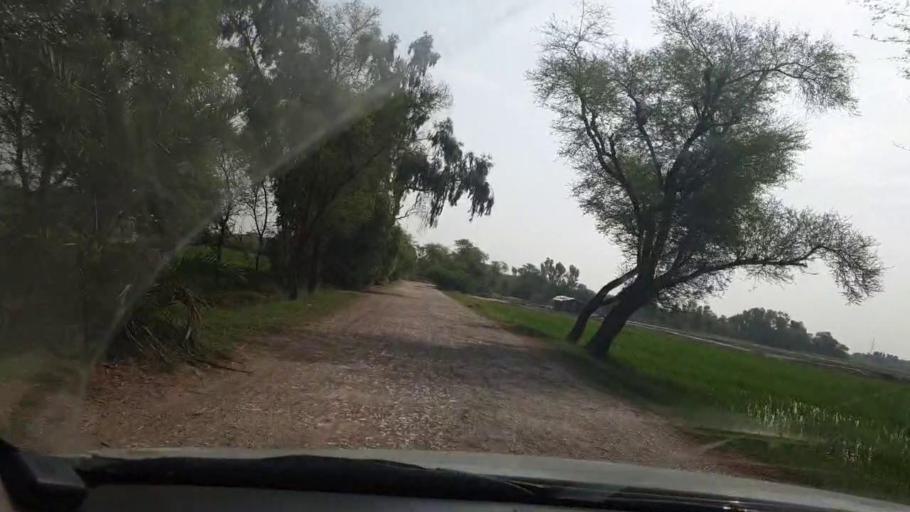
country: PK
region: Sindh
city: Lakhi
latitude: 27.8307
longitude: 68.7559
